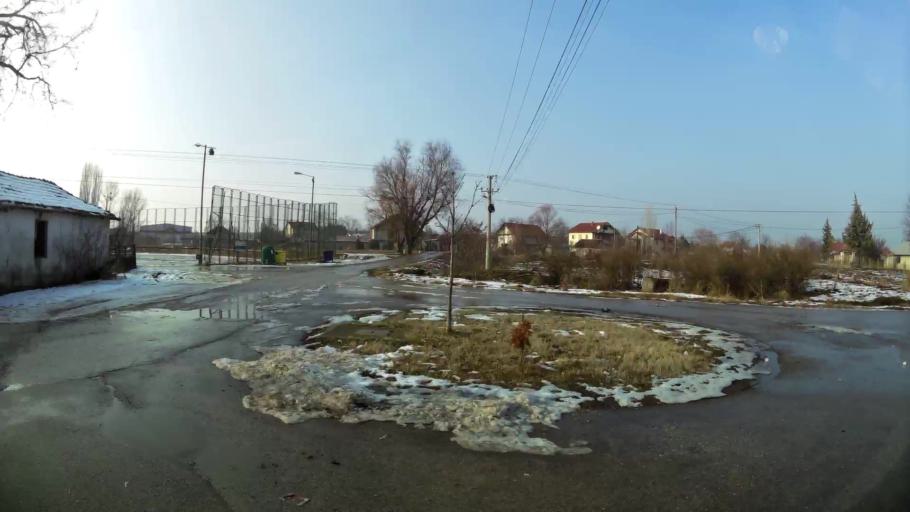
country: MK
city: Miladinovci
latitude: 41.9791
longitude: 21.6500
